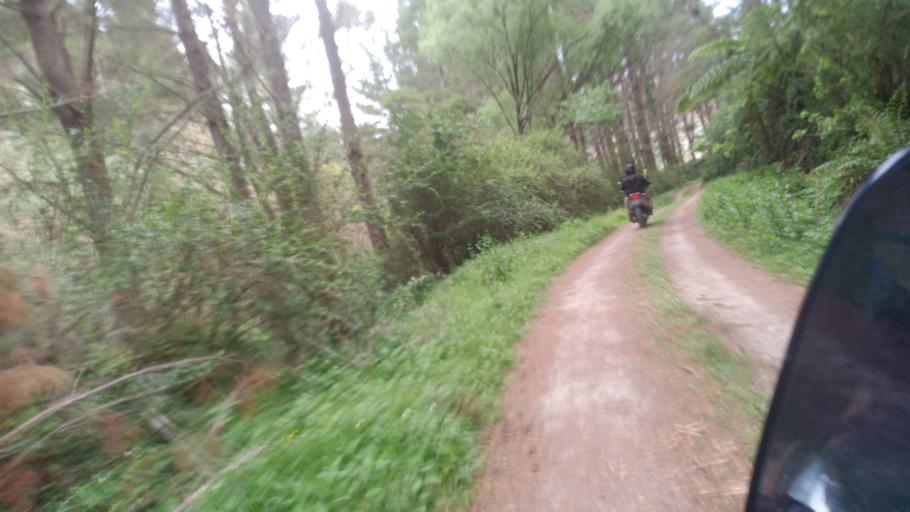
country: NZ
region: Gisborne
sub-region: Gisborne District
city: Gisborne
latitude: -38.4602
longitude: 177.9093
